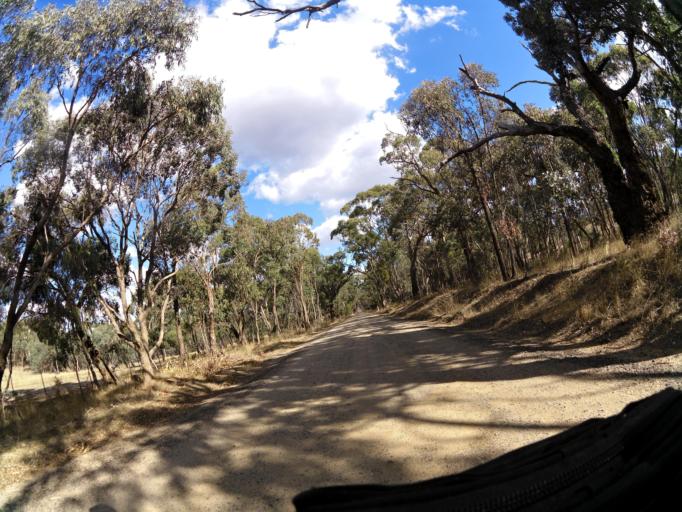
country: AU
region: Victoria
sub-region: Greater Bendigo
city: Kennington
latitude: -36.9987
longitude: 144.8122
